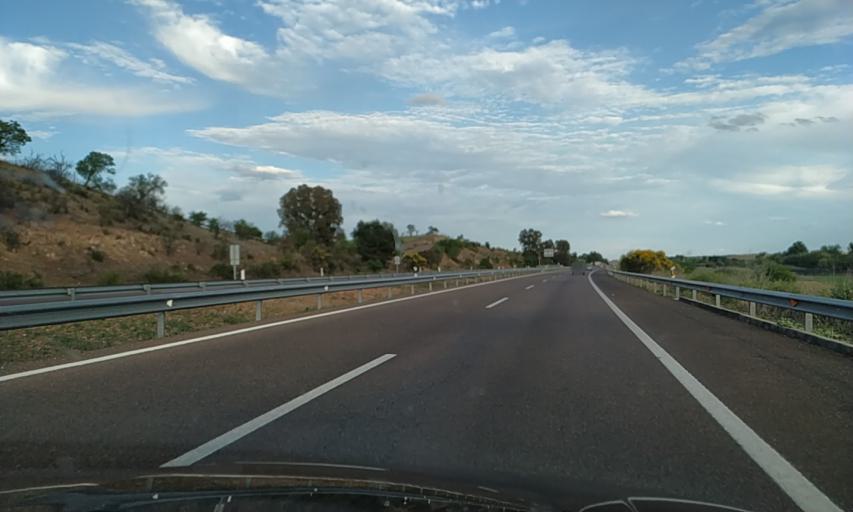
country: ES
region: Extremadura
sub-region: Provincia de Badajoz
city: Valdelacalzada
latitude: 38.8477
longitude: -6.6807
